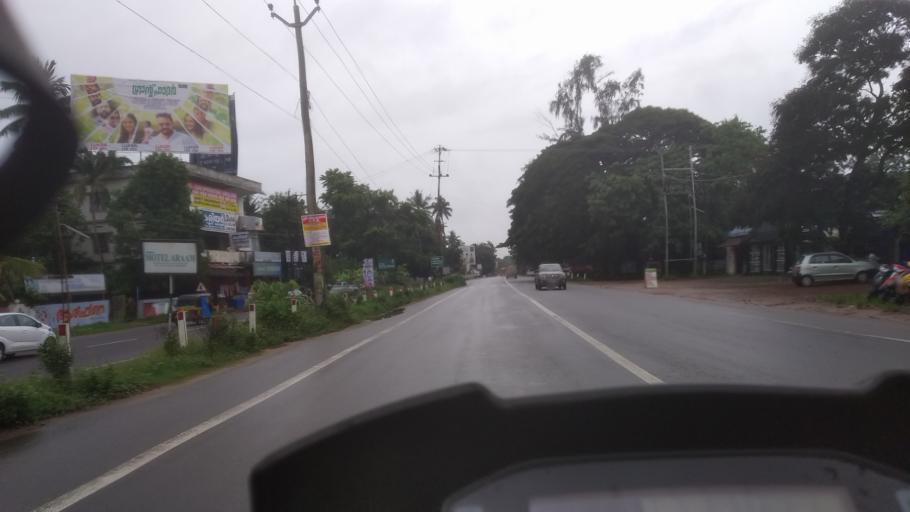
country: IN
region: Kerala
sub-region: Alappuzha
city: Kayankulam
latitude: 9.1386
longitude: 76.5121
